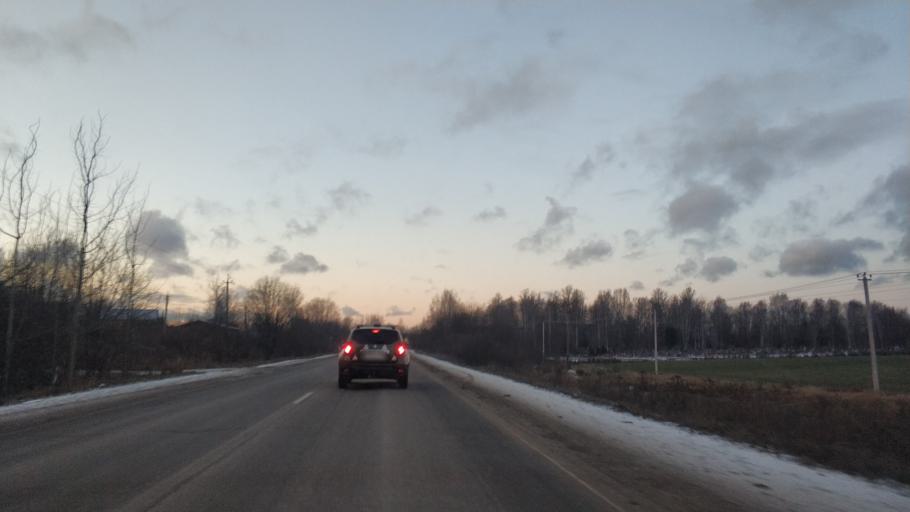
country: RU
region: St.-Petersburg
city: Pontonnyy
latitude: 59.8050
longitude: 30.6256
